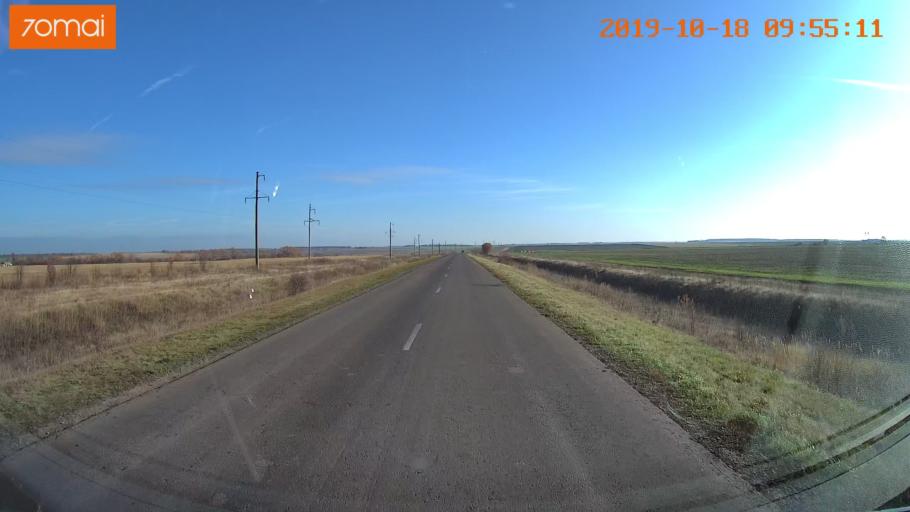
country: RU
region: Tula
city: Kazachka
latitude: 53.3690
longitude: 38.3582
